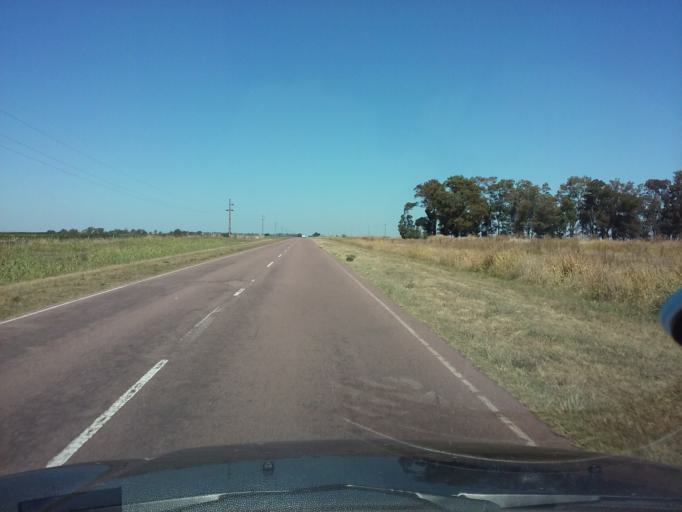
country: AR
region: La Pampa
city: Colonia Baron
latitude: -36.2710
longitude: -63.9429
